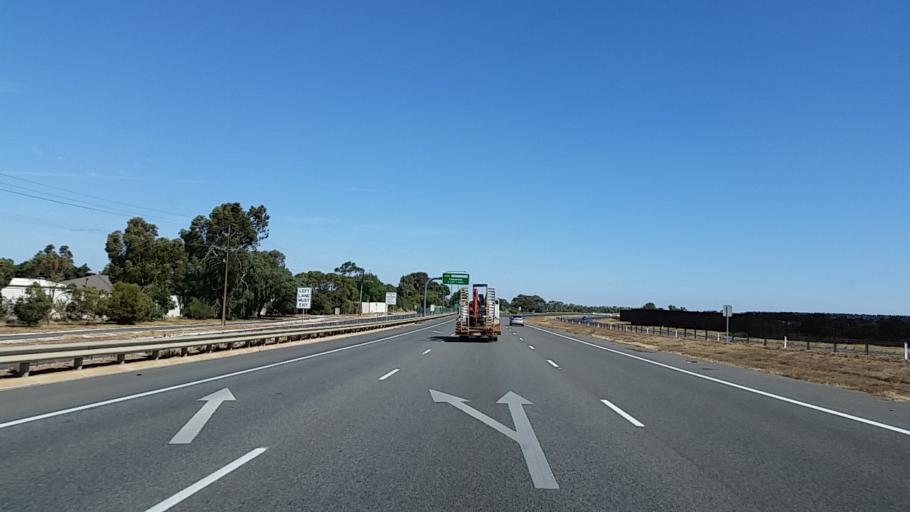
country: AU
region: South Australia
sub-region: Gawler
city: Gawler
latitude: -34.5953
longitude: 138.7295
